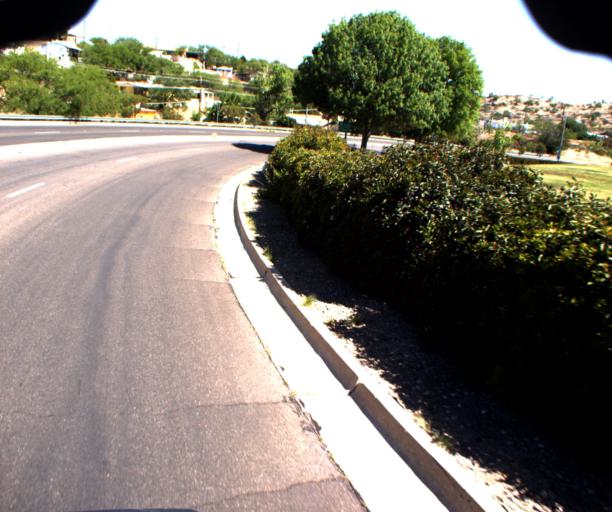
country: US
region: Arizona
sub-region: Santa Cruz County
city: Nogales
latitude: 31.3500
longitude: -110.9289
